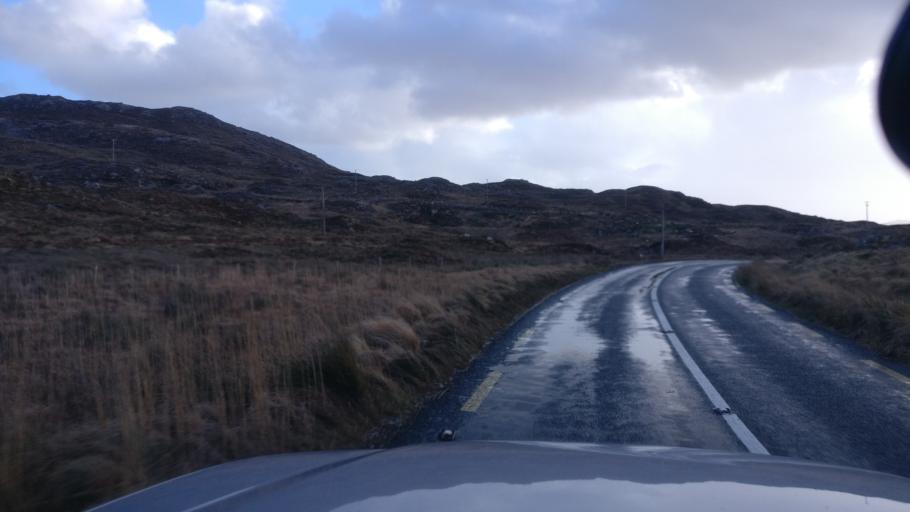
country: IE
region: Connaught
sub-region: County Galway
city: Clifden
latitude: 53.4311
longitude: -9.7676
